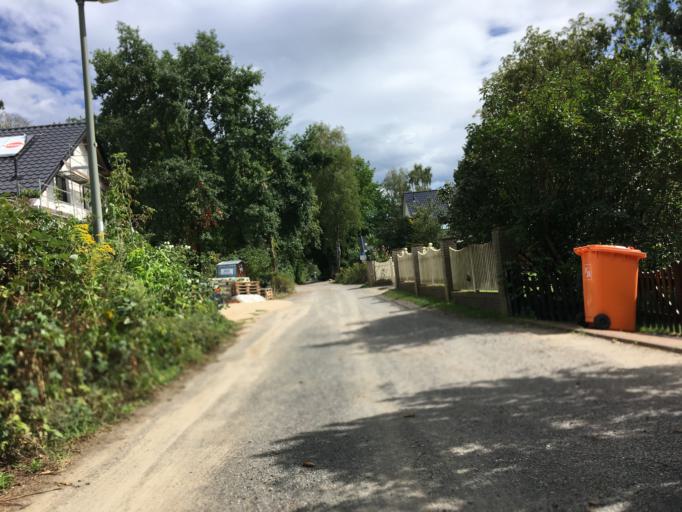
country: DE
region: Berlin
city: Staaken
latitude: 52.5197
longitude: 13.1334
